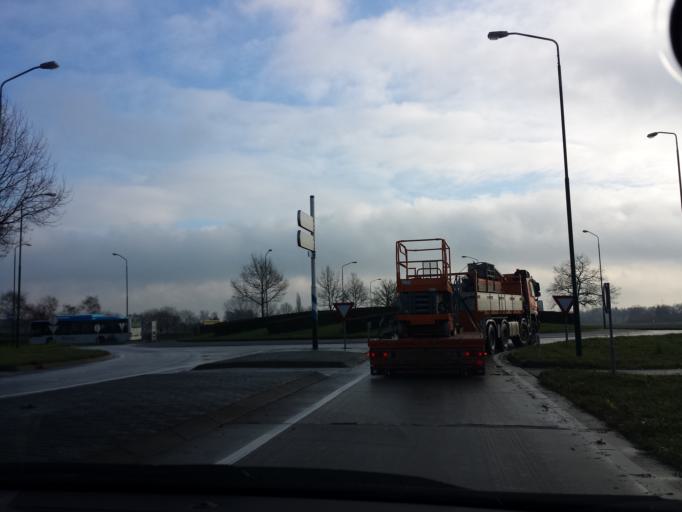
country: NL
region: North Brabant
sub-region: Gemeente Landerd
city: Zeeland
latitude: 51.7065
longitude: 5.6812
